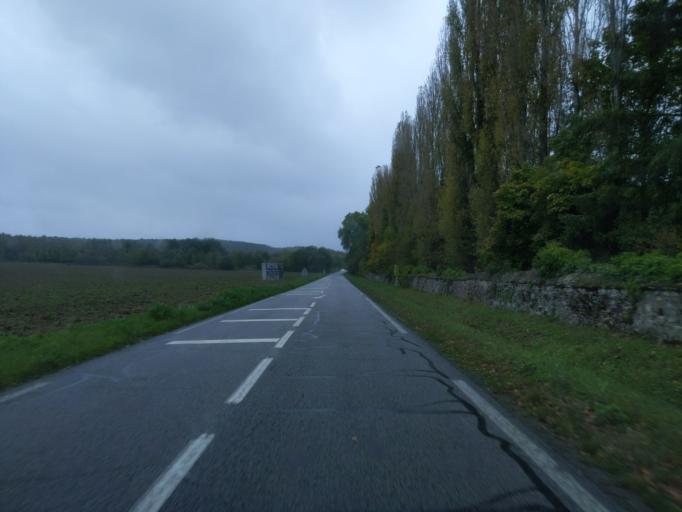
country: FR
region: Ile-de-France
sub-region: Departement des Yvelines
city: Dampierre-en-Yvelines
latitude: 48.6916
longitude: 1.9750
